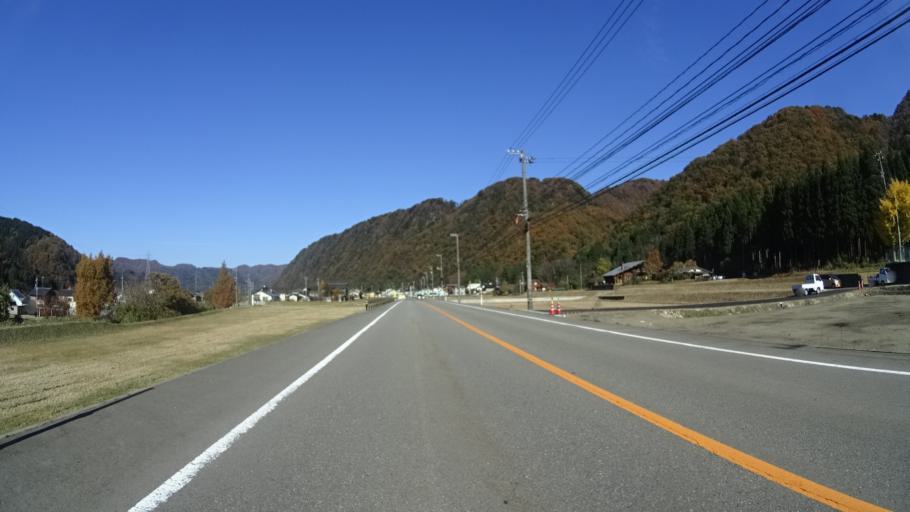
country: JP
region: Ishikawa
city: Tsurugi-asahimachi
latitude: 36.3554
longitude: 136.6241
